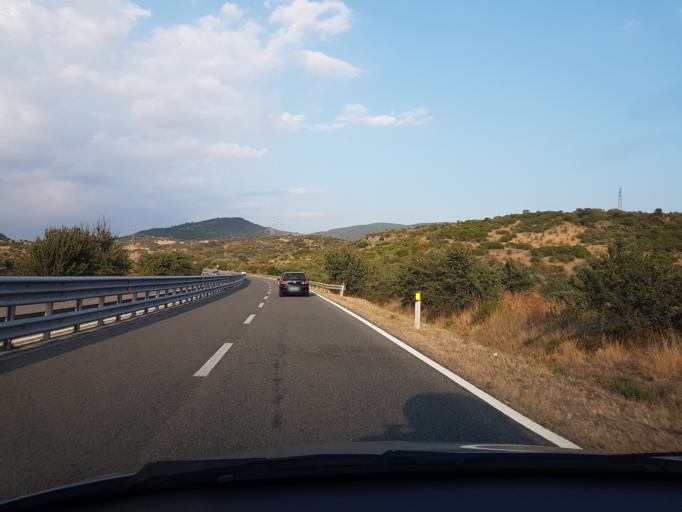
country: IT
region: Sardinia
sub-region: Provincia di Nuoro
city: Orotelli
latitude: 40.2642
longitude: 9.1156
